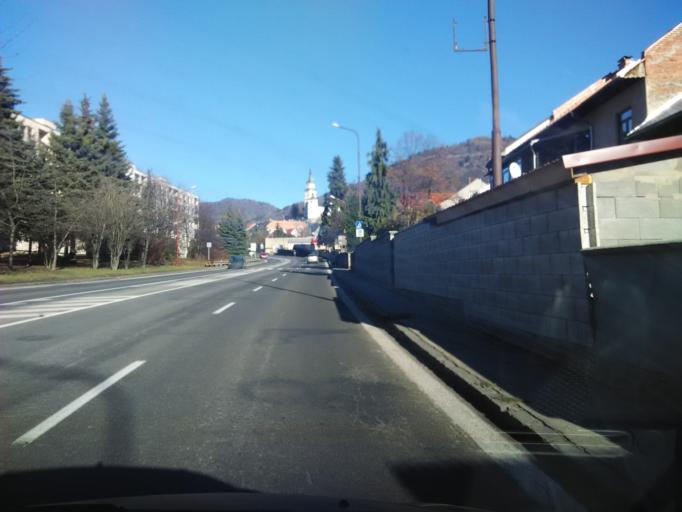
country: SK
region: Banskobystricky
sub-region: Okres Ziar nad Hronom
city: Kremnica
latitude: 48.7007
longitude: 18.9143
